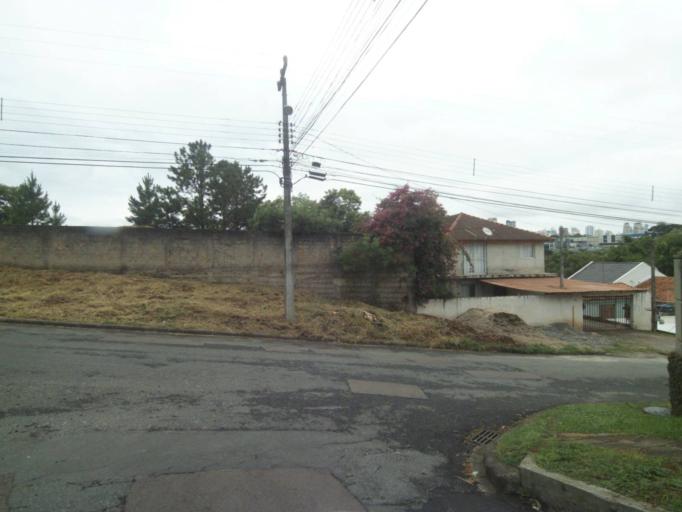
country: BR
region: Parana
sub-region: Curitiba
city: Curitiba
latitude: -25.4273
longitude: -49.3198
